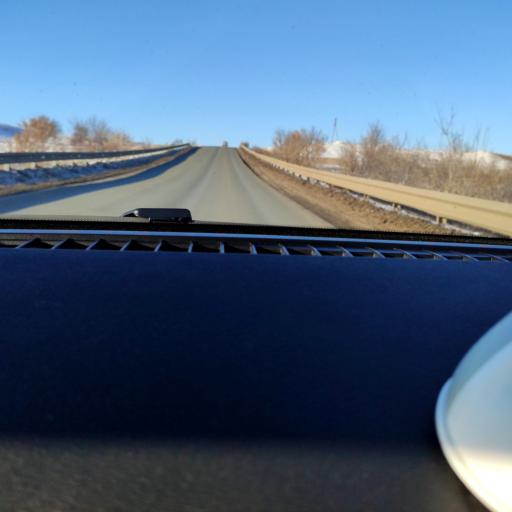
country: RU
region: Samara
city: Spiridonovka
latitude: 53.1437
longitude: 50.5864
